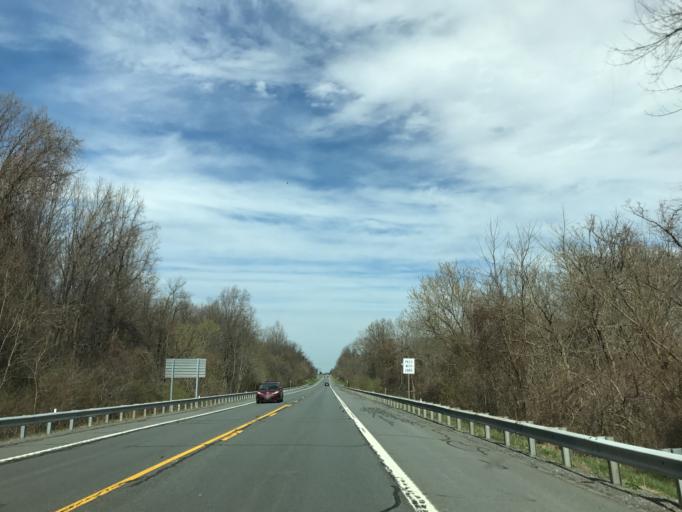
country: US
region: Maryland
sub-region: Frederick County
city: Point of Rocks
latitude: 39.2928
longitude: -77.5269
